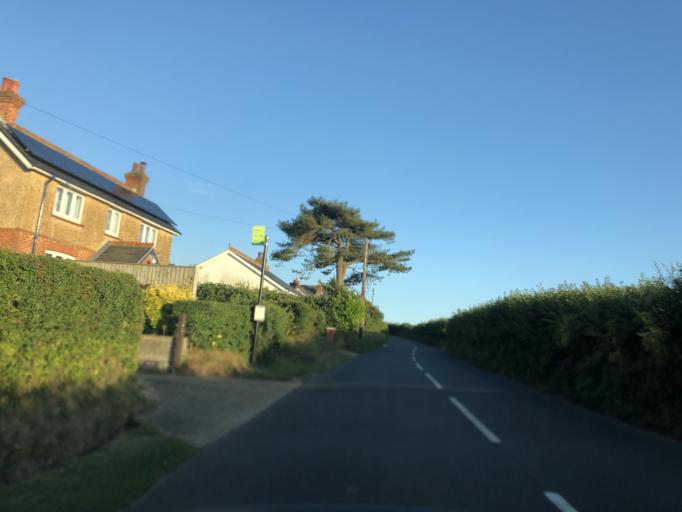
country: GB
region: England
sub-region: Isle of Wight
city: Chale
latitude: 50.6084
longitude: -1.3191
